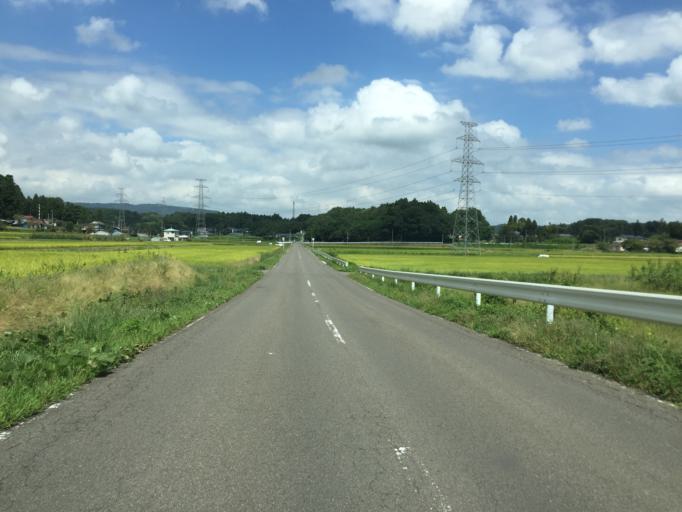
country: JP
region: Fukushima
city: Motomiya
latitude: 37.5630
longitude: 140.3840
